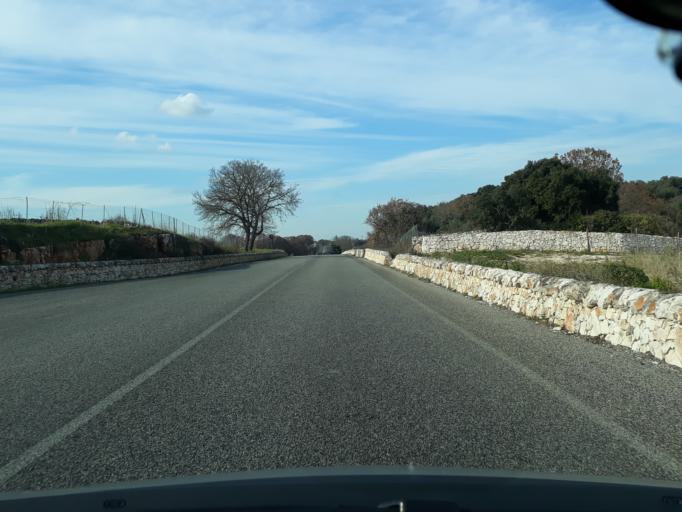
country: IT
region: Apulia
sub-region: Provincia di Bari
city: Locorotondo
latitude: 40.7592
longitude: 17.3399
